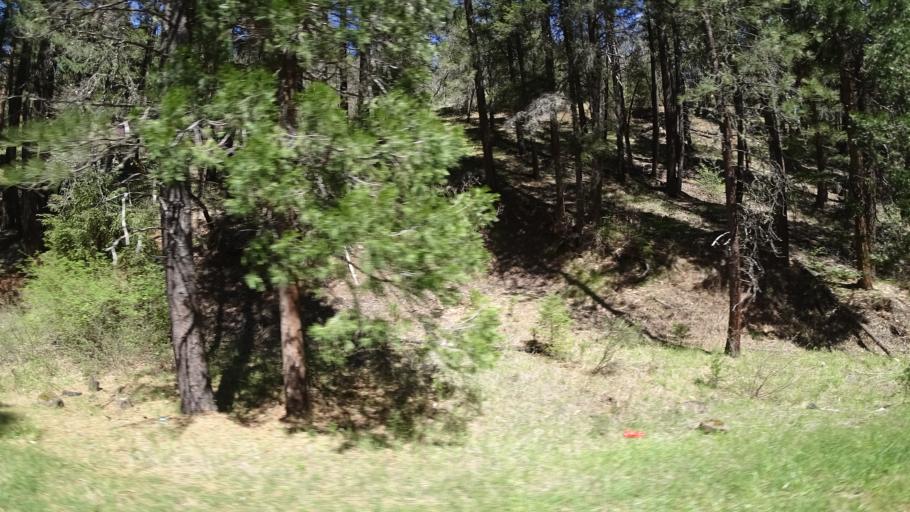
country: US
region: California
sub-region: Trinity County
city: Weaverville
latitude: 40.7653
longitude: -122.8889
